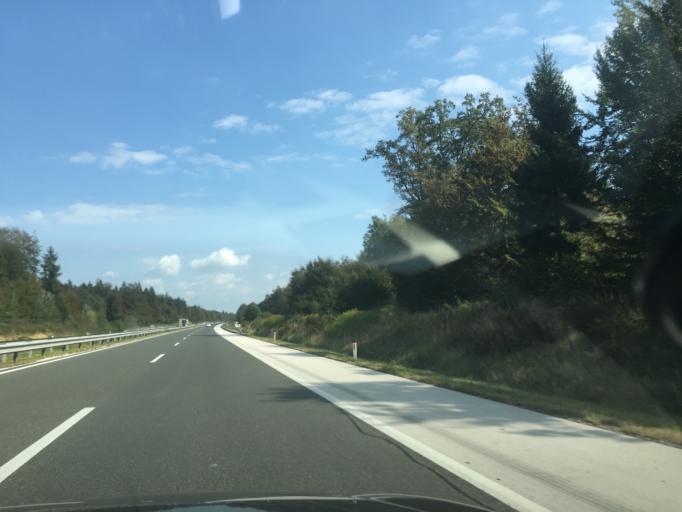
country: SI
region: Krsko
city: Leskovec pri Krskem
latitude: 45.9114
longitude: 15.4124
